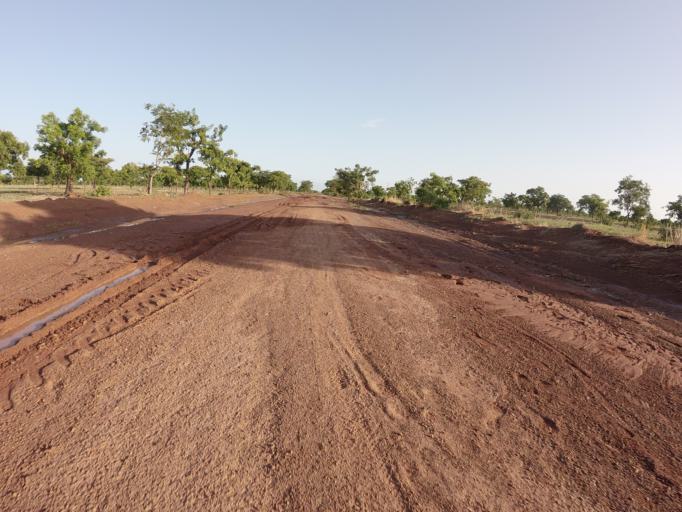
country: TG
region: Savanes
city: Sansanne-Mango
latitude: 10.3647
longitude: -0.0937
